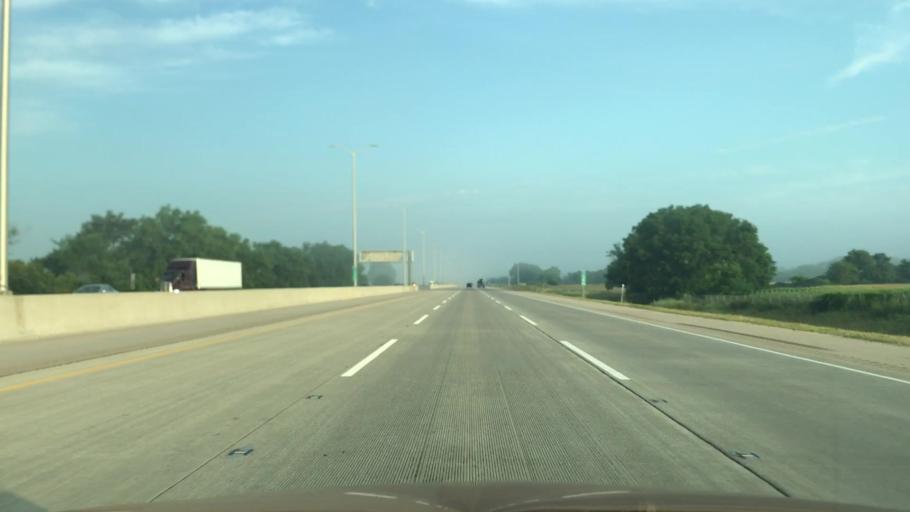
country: US
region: Illinois
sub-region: Kane County
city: Hampshire
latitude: 42.1560
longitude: -88.5528
